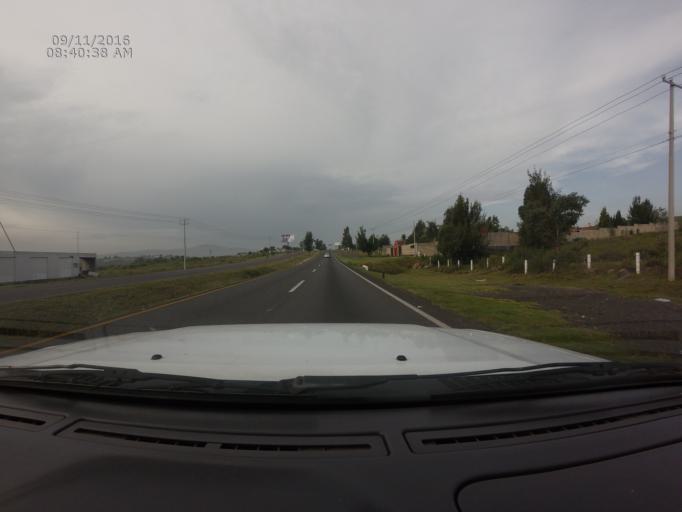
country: MX
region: Michoacan
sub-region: Morelia
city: La Mintzita (Piedra Dura)
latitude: 19.6075
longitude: -101.2872
